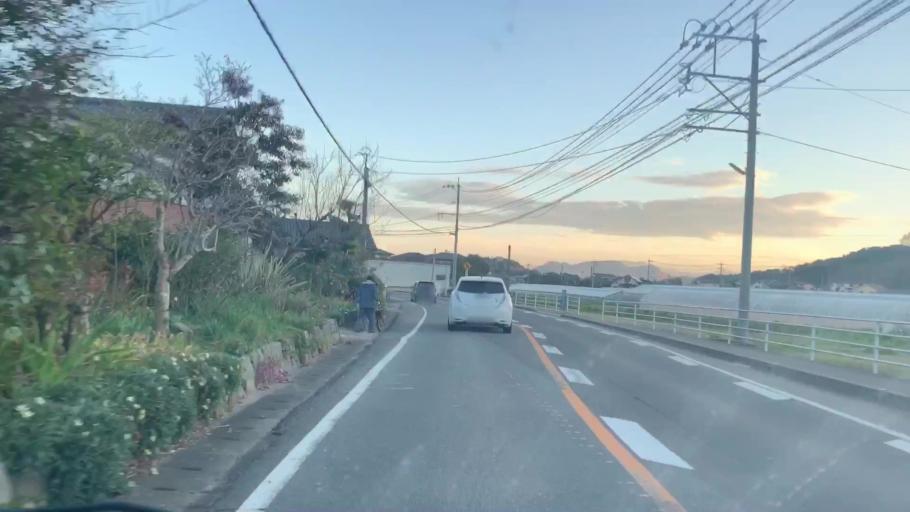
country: JP
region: Saga Prefecture
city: Takeocho-takeo
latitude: 33.2229
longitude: 130.0259
